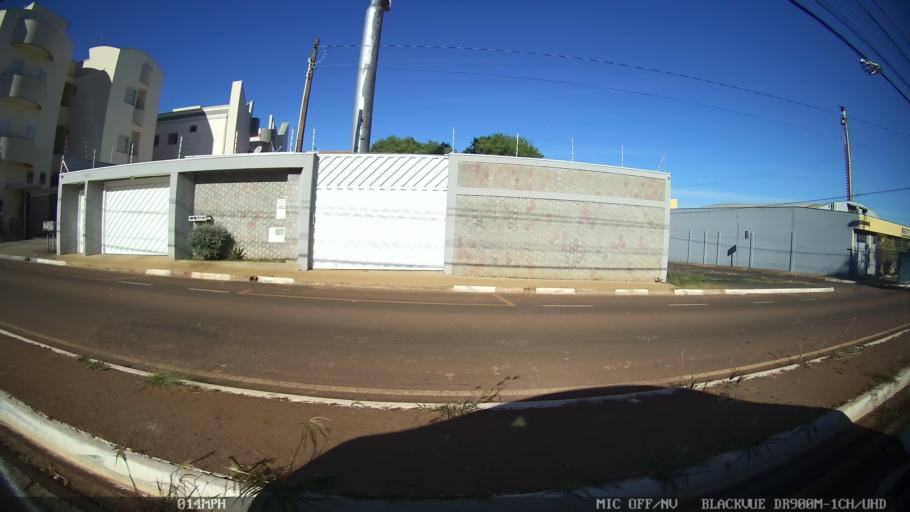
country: BR
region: Sao Paulo
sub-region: Franca
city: Franca
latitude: -20.5649
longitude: -47.4043
